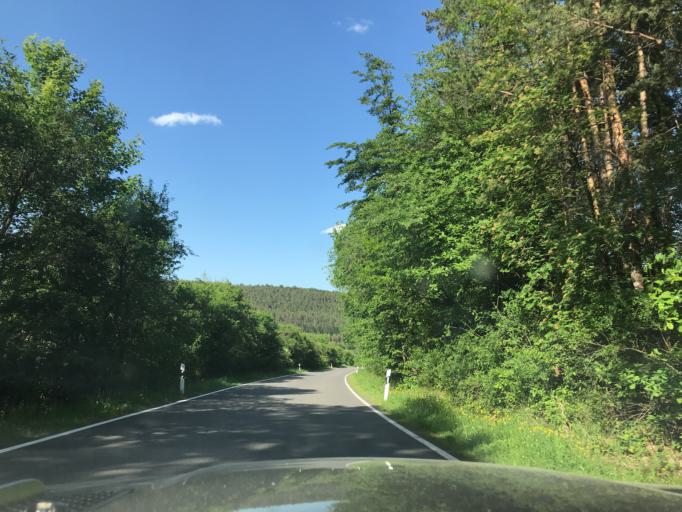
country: DE
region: Thuringia
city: Behringen
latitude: 50.7823
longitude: 10.9714
